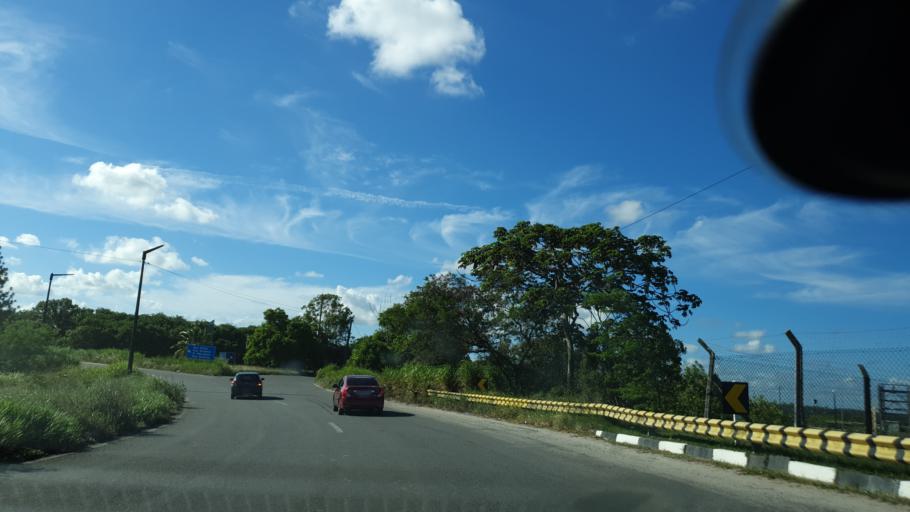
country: BR
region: Bahia
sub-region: Camacari
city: Camacari
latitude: -12.6585
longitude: -38.3014
